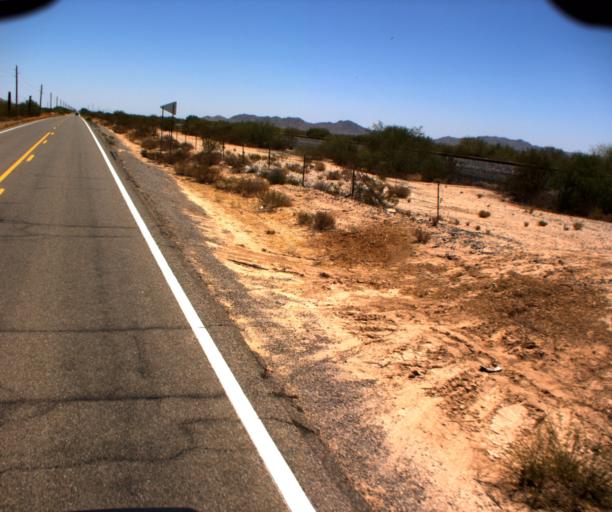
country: US
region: Arizona
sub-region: Pinal County
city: Maricopa
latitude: 33.0575
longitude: -112.2635
